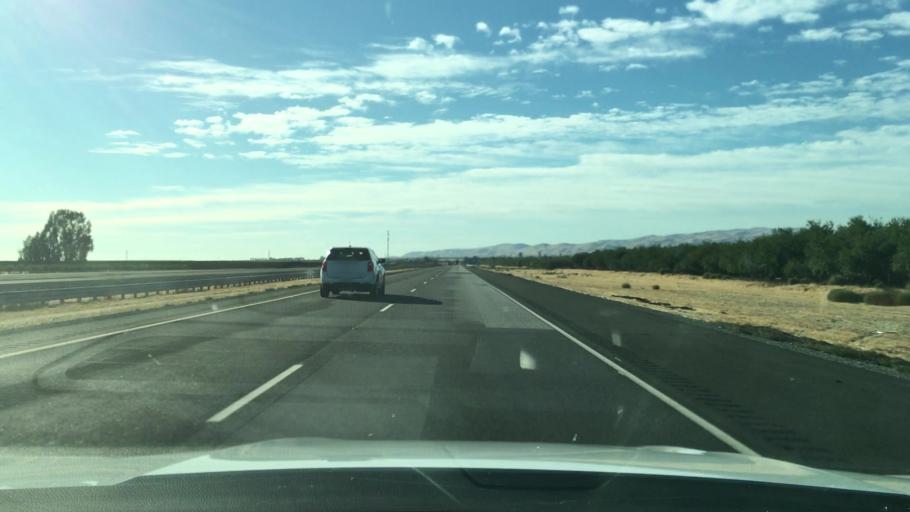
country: US
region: California
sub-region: Fresno County
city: Firebaugh
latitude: 36.6542
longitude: -120.6348
